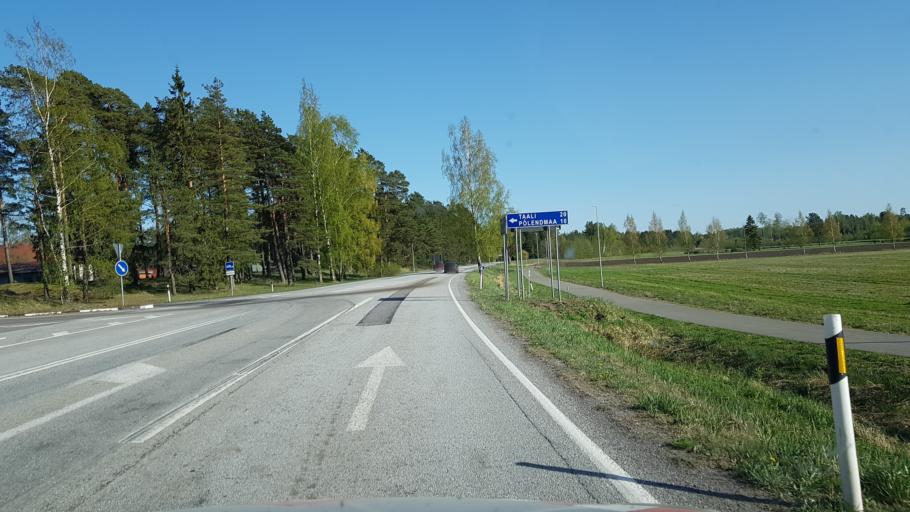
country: EE
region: Paernumaa
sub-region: Paikuse vald
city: Paikuse
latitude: 58.3578
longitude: 24.6597
